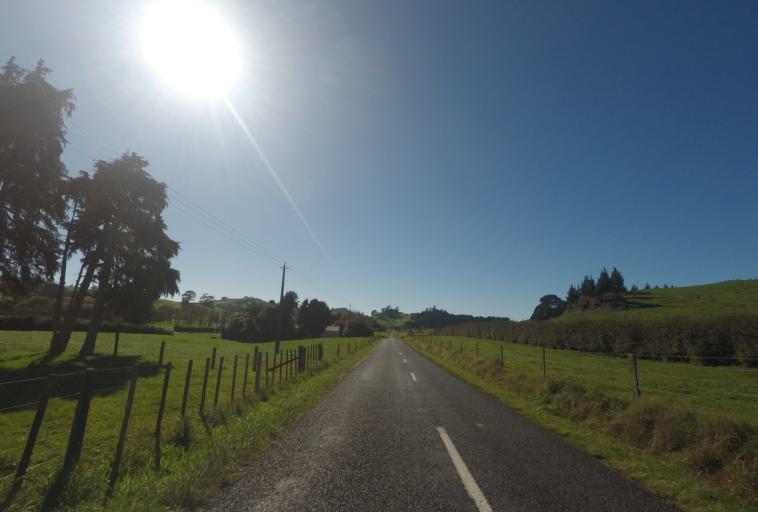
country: NZ
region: Bay of Plenty
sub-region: Western Bay of Plenty District
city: Waihi Beach
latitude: -37.4108
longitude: 175.8937
